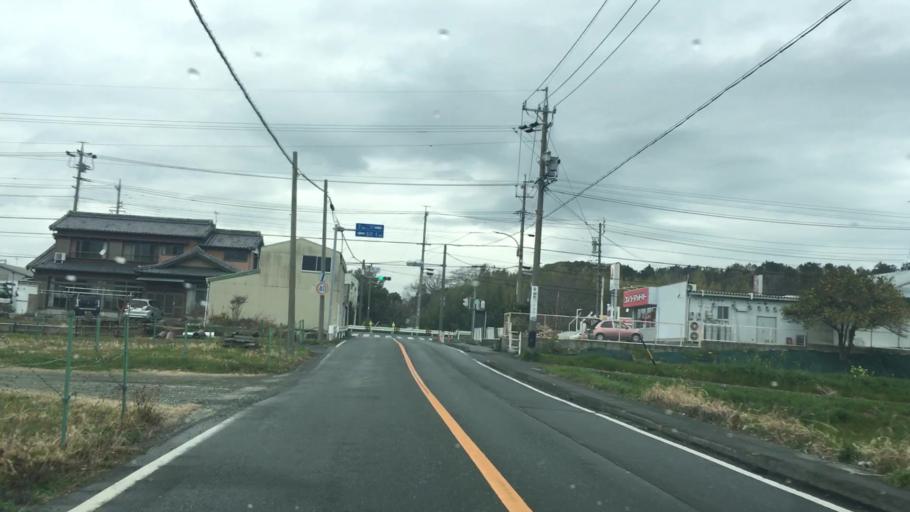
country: JP
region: Aichi
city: Toyohashi
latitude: 34.7228
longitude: 137.4178
